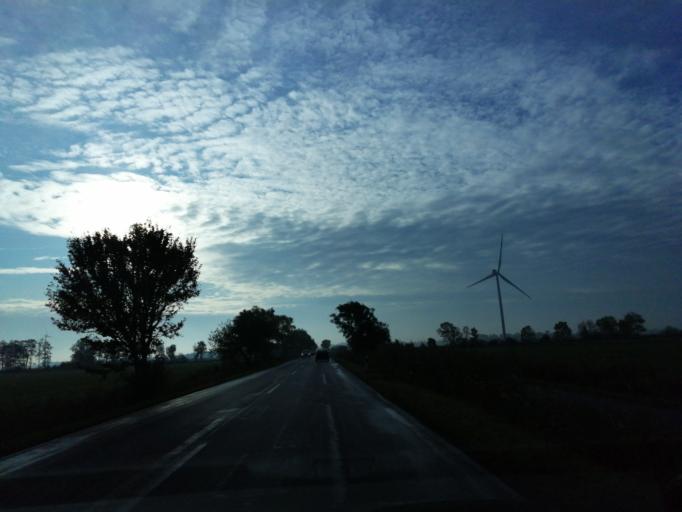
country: DE
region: Lower Saxony
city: Fedderwarden
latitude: 53.6130
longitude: 8.0405
